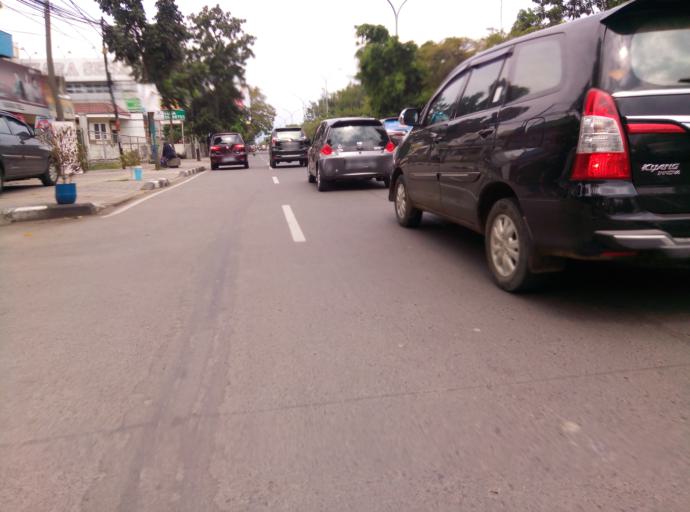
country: ID
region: West Java
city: Bandung
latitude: -6.9352
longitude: 107.6426
